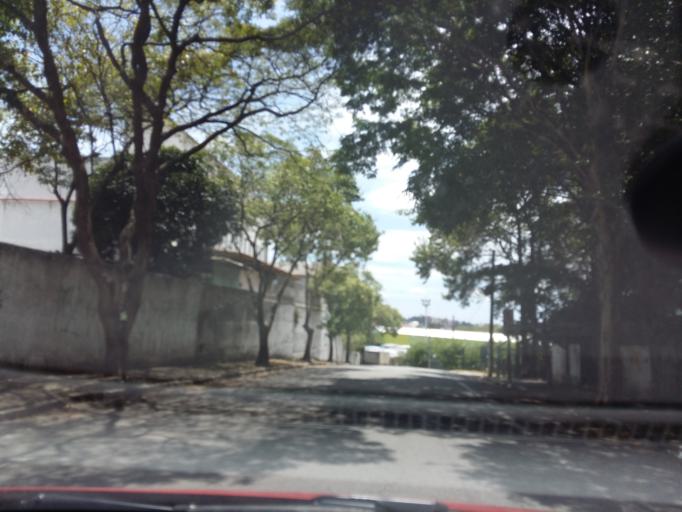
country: BR
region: Sao Paulo
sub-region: Sao Caetano Do Sul
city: Sao Caetano do Sul
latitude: -23.6295
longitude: -46.5985
